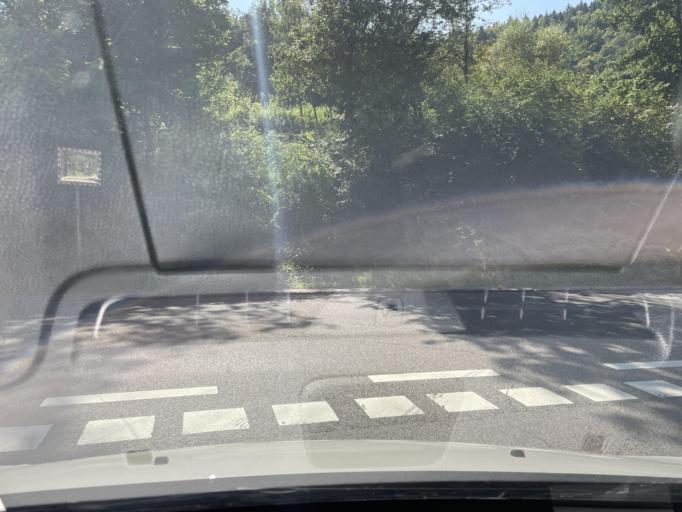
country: DE
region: Saarland
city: Sankt Ingbert
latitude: 49.2678
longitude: 7.1349
